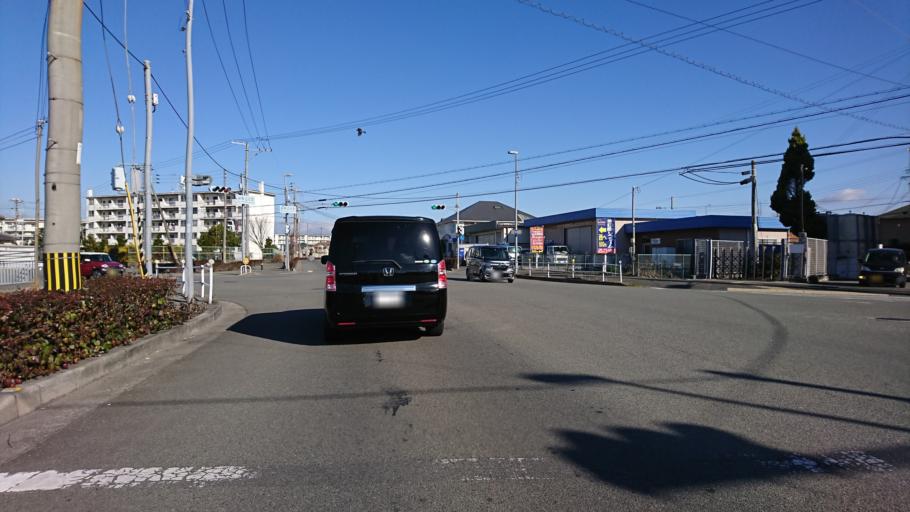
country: JP
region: Hyogo
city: Kakogawacho-honmachi
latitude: 34.7382
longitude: 134.8421
